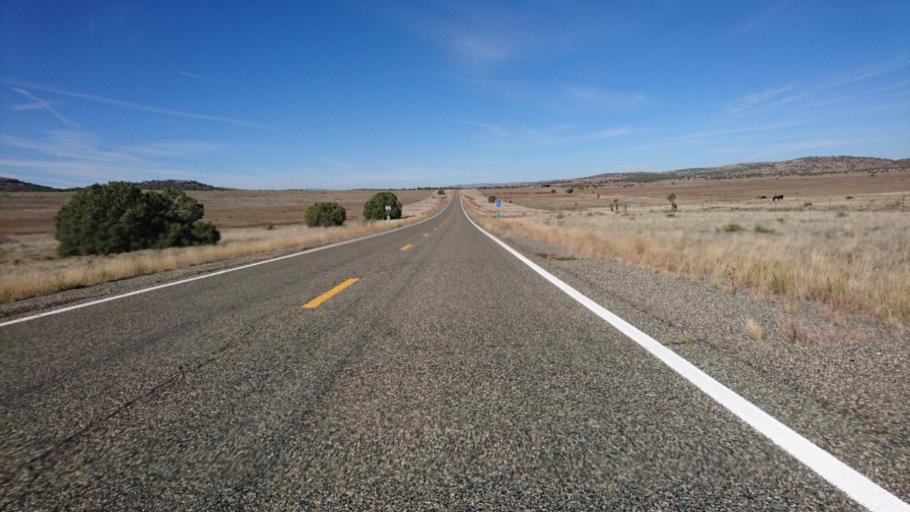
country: US
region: Arizona
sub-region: Yavapai County
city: Paulden
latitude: 35.2841
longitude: -112.7177
